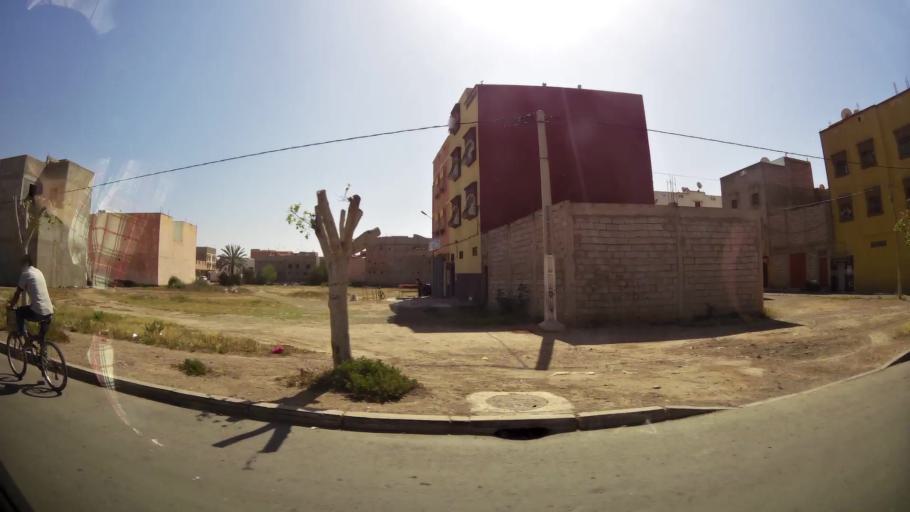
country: MA
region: Souss-Massa-Draa
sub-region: Inezgane-Ait Mellou
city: Inezgane
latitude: 30.3430
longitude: -9.5080
